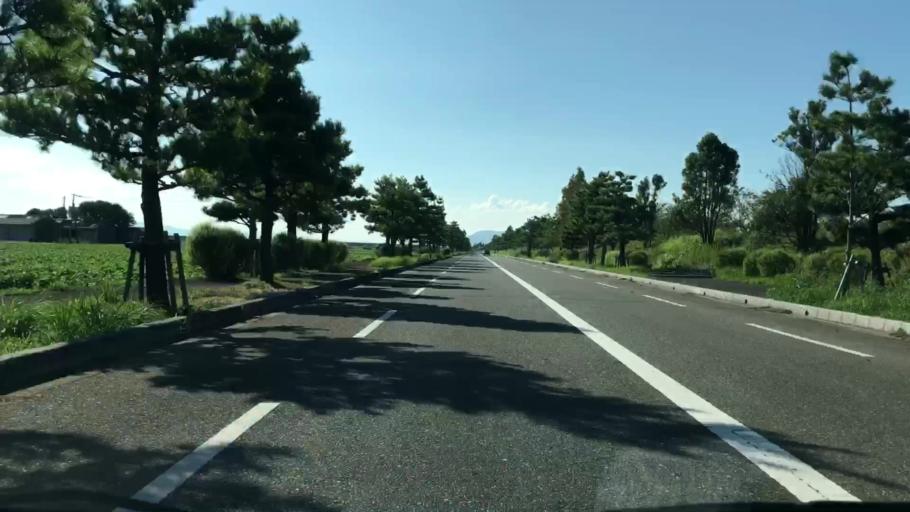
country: JP
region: Saga Prefecture
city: Okawa
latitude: 33.1568
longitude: 130.2981
